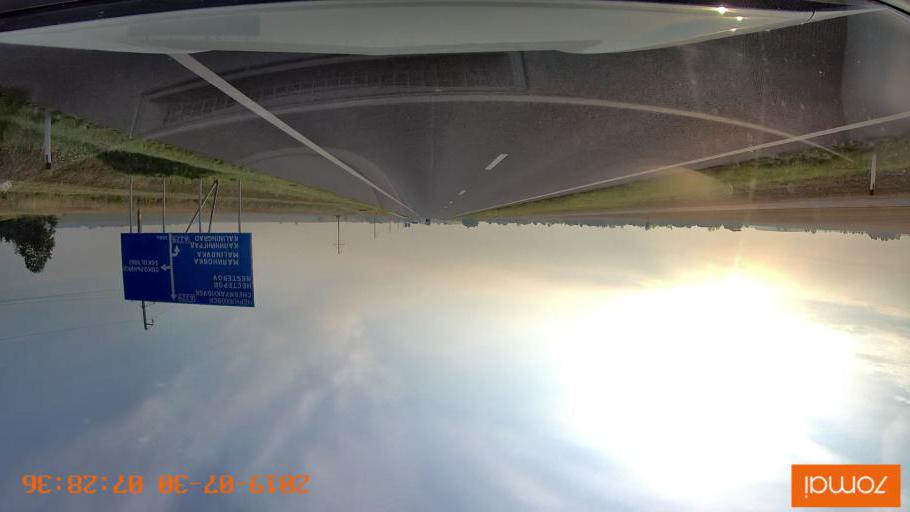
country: RU
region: Kaliningrad
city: Gvardeysk
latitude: 54.6765
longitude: 20.9178
